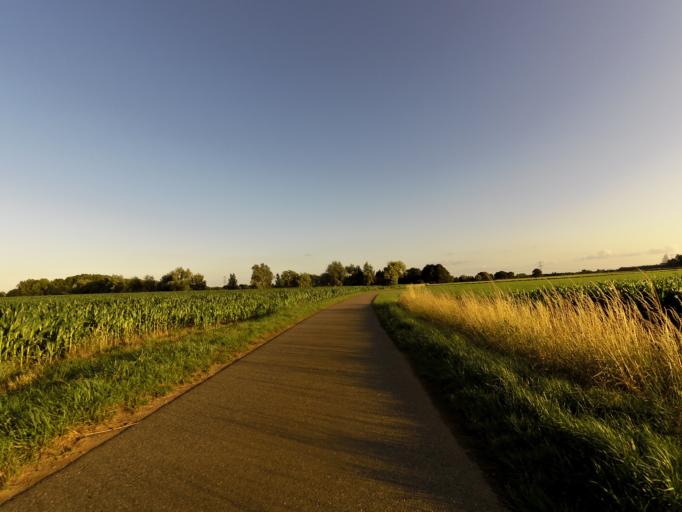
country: NL
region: Gelderland
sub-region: Gemeente Doesburg
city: Doesburg
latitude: 51.9902
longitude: 6.2082
